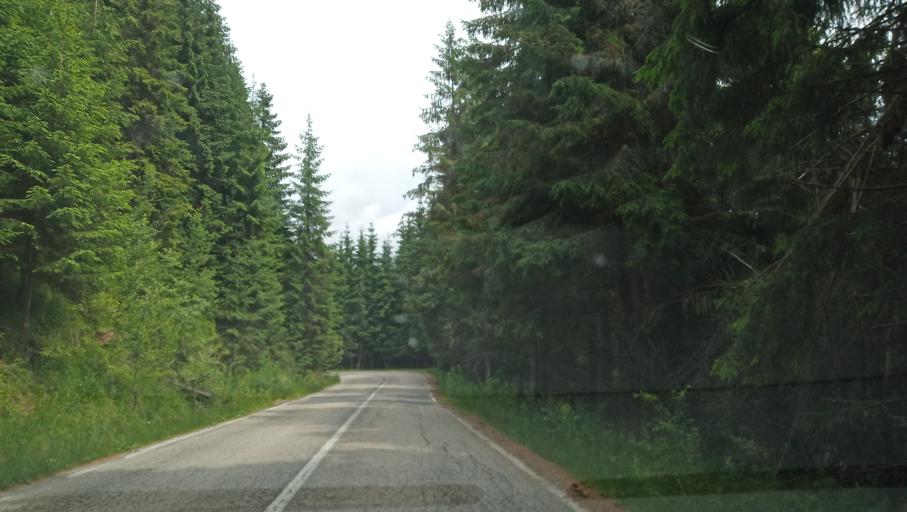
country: RO
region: Valcea
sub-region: Comuna Voineasa
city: Voineasa
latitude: 45.4239
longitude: 23.7478
